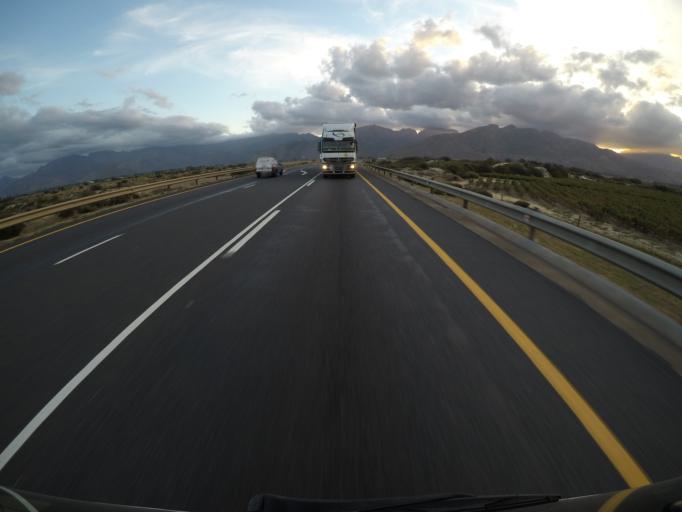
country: ZA
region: Western Cape
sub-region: Cape Winelands District Municipality
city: Worcester
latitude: -33.6411
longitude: 19.3113
